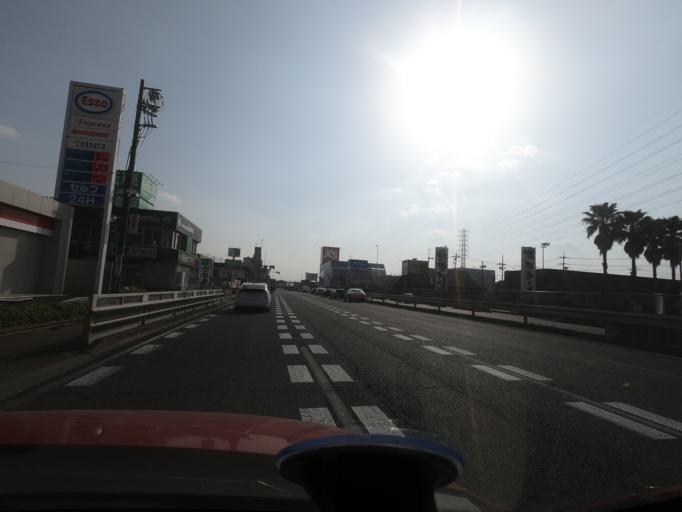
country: JP
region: Aichi
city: Kasugai
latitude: 35.2626
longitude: 136.9889
